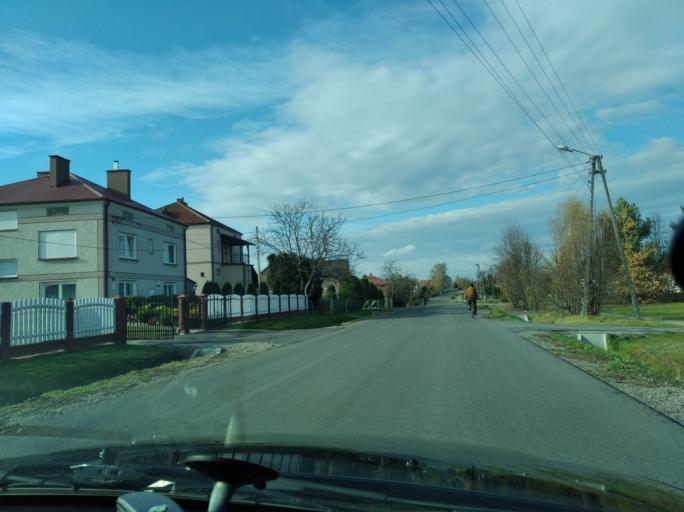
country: PL
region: Subcarpathian Voivodeship
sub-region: Powiat ropczycko-sedziszowski
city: Iwierzyce
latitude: 50.0758
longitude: 21.7479
